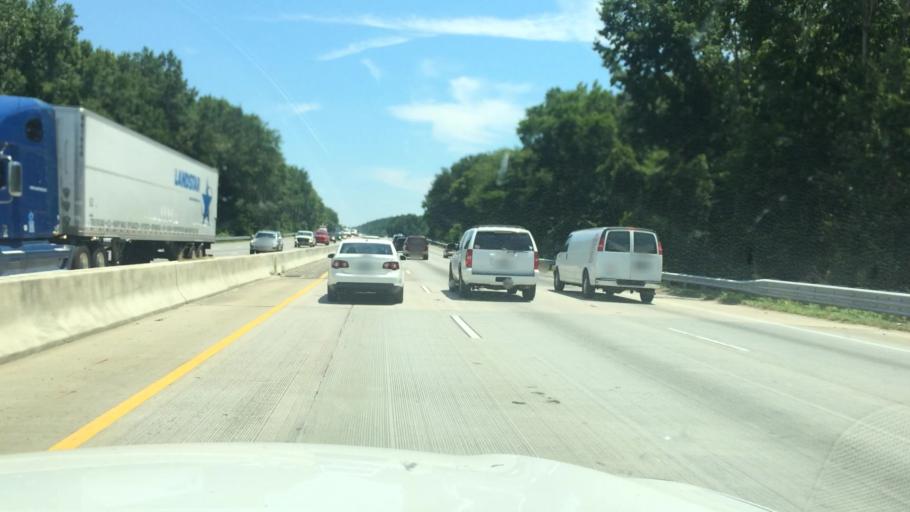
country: US
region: South Carolina
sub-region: Lexington County
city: West Columbia
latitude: 34.0487
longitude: -81.0715
